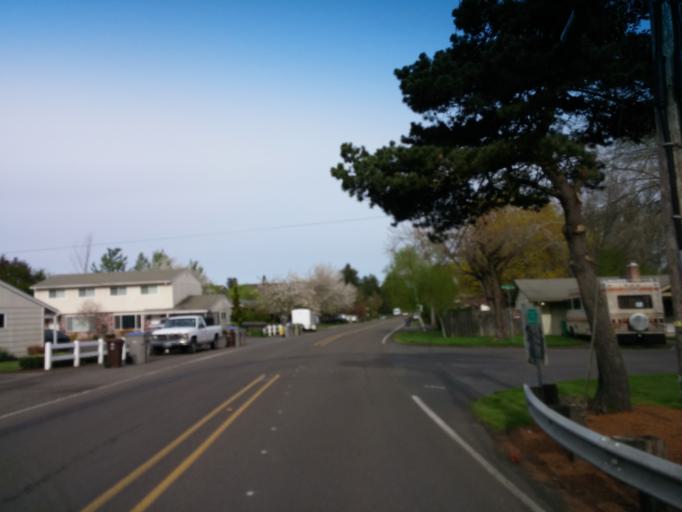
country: US
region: Oregon
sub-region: Washington County
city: Cedar Hills
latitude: 45.5135
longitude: -122.8062
